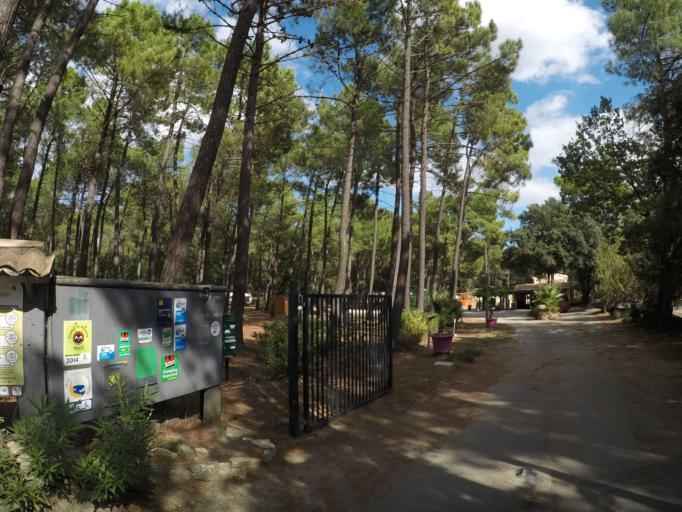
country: FR
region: Provence-Alpes-Cote d'Azur
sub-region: Departement du Vaucluse
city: Bollene
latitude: 44.2968
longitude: 4.7867
